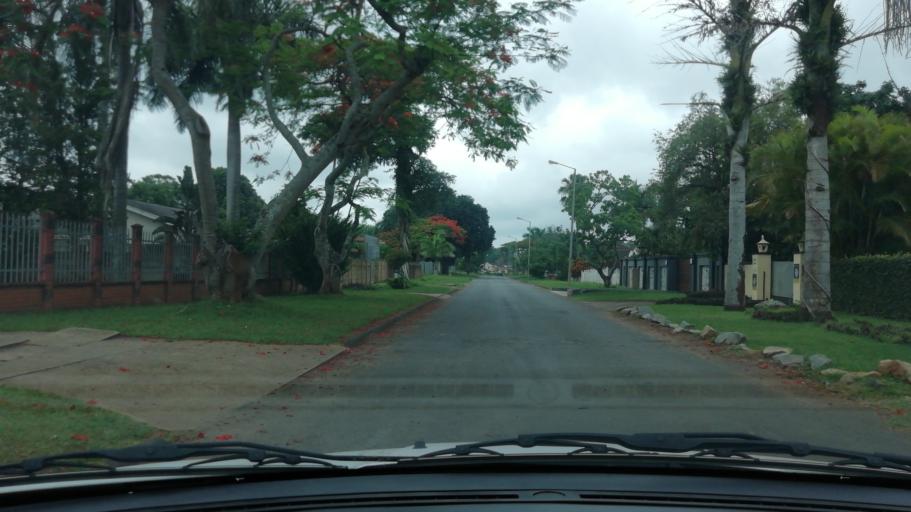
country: ZA
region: KwaZulu-Natal
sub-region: uThungulu District Municipality
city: Empangeni
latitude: -28.7609
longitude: 31.8998
